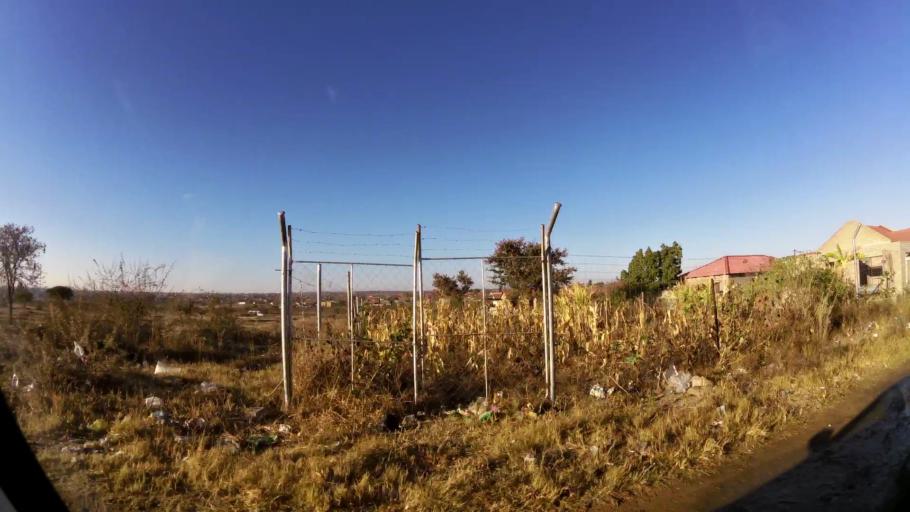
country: ZA
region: Limpopo
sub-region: Capricorn District Municipality
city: Polokwane
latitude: -23.8392
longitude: 29.3572
